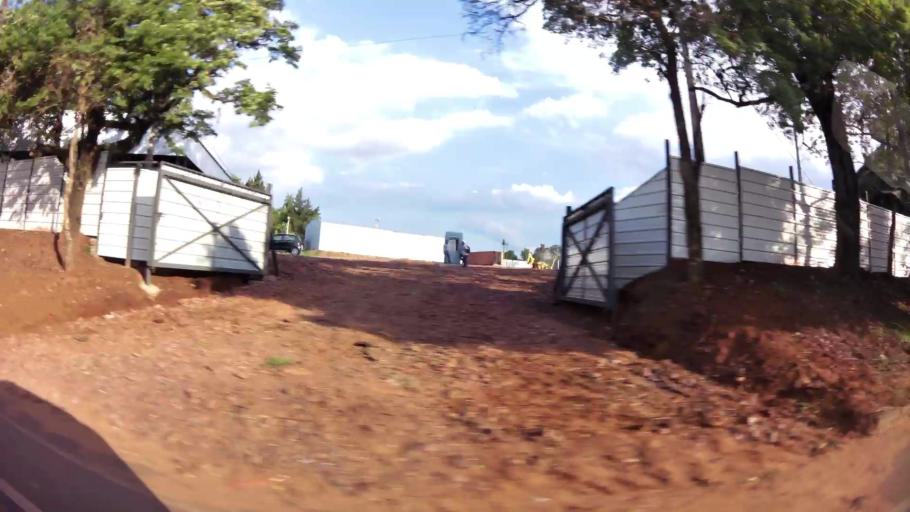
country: PY
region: Central
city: Fernando de la Mora
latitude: -25.3516
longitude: -57.5330
